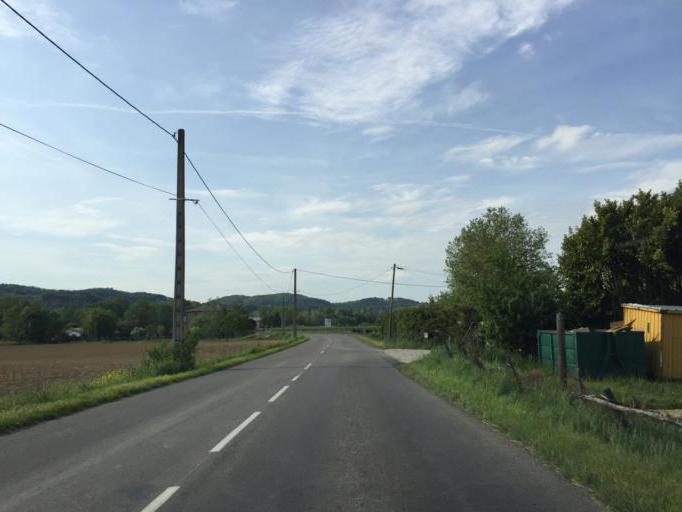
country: FR
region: Rhone-Alpes
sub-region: Departement de la Drome
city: Peyrins
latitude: 45.0773
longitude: 5.0400
